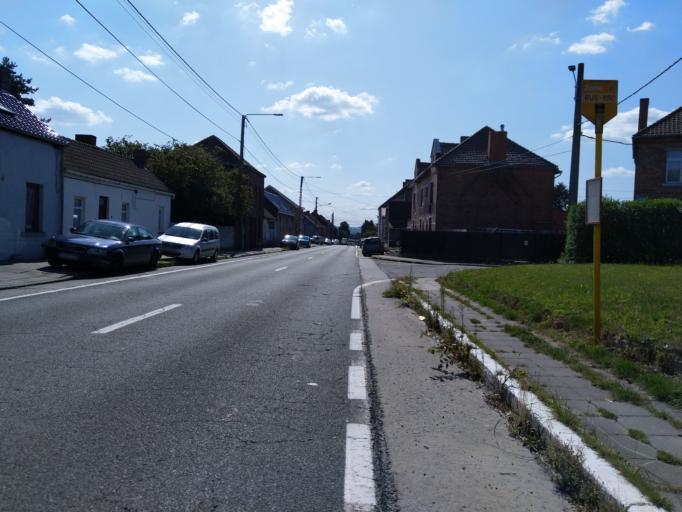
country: BE
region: Wallonia
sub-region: Province du Hainaut
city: Saint-Ghislain
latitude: 50.4898
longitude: 3.8322
